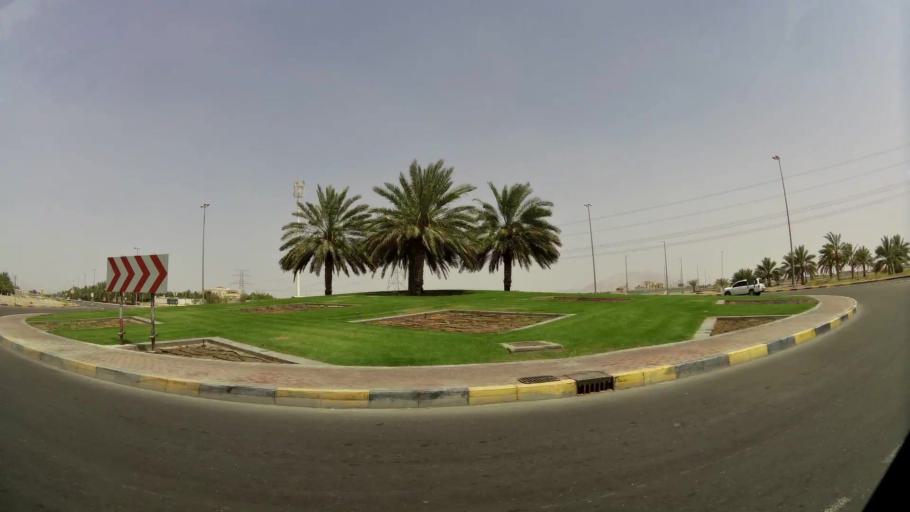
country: AE
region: Abu Dhabi
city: Al Ain
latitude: 24.1847
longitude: 55.6790
